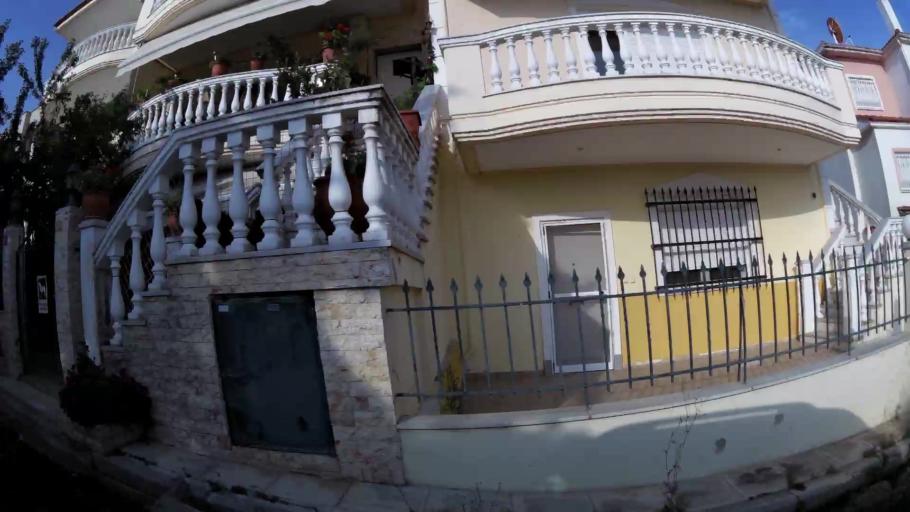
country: GR
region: Central Macedonia
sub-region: Nomos Thessalonikis
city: Oraiokastro
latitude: 40.7197
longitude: 22.9017
